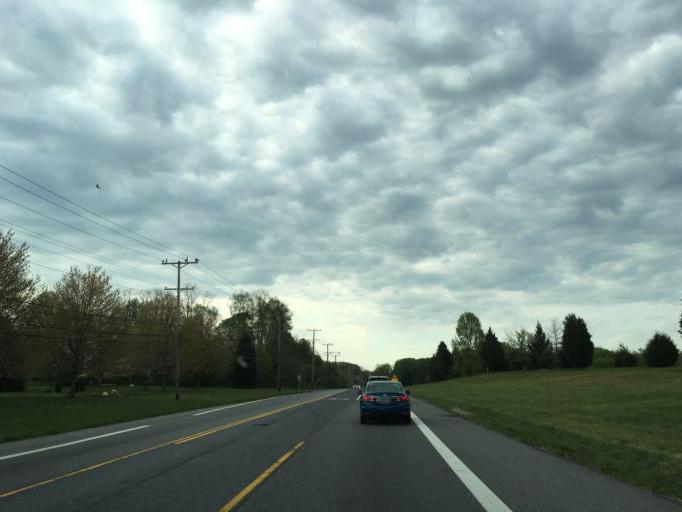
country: US
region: Maryland
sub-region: Carroll County
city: Sykesville
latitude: 39.3390
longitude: -76.9537
